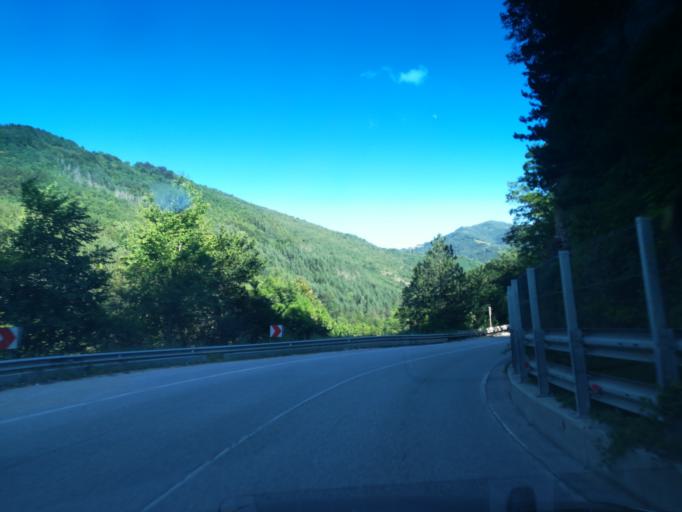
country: BG
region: Smolyan
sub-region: Obshtina Chepelare
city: Chepelare
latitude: 41.8177
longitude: 24.6999
